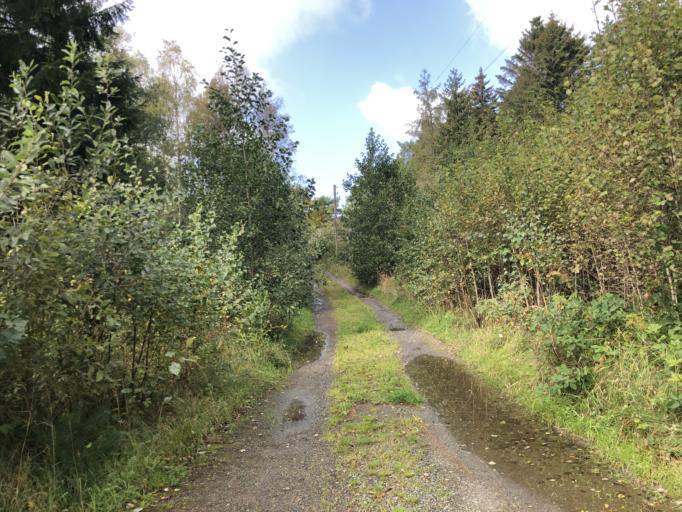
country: SE
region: Vaestra Goetaland
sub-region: Goteborg
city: Majorna
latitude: 57.7360
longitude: 11.8582
